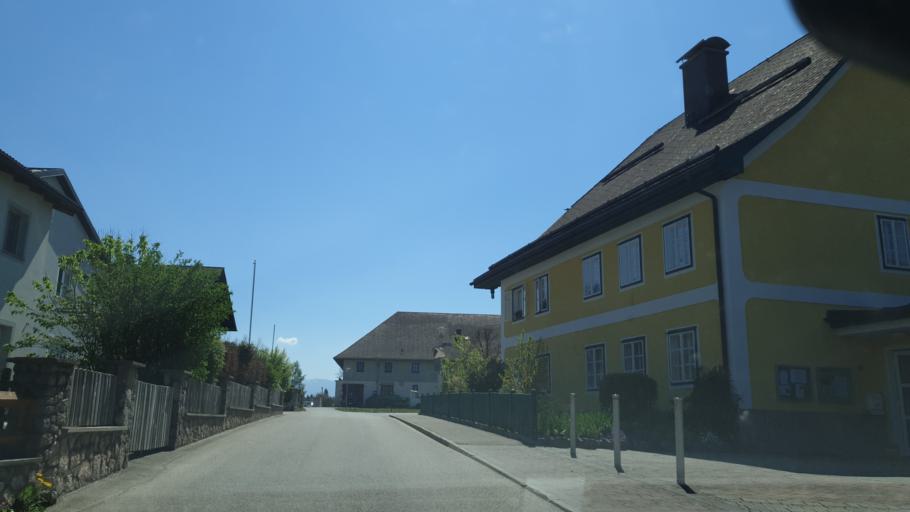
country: AT
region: Upper Austria
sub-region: Politischer Bezirk Vocklabruck
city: Gampern
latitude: 47.9901
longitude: 13.5560
